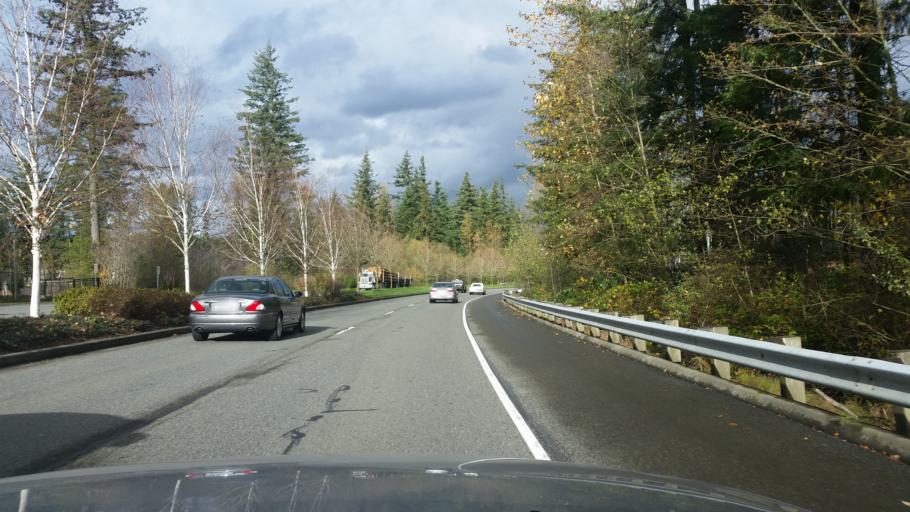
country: US
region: Washington
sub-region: King County
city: Fall City
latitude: 47.5246
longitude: -121.8797
